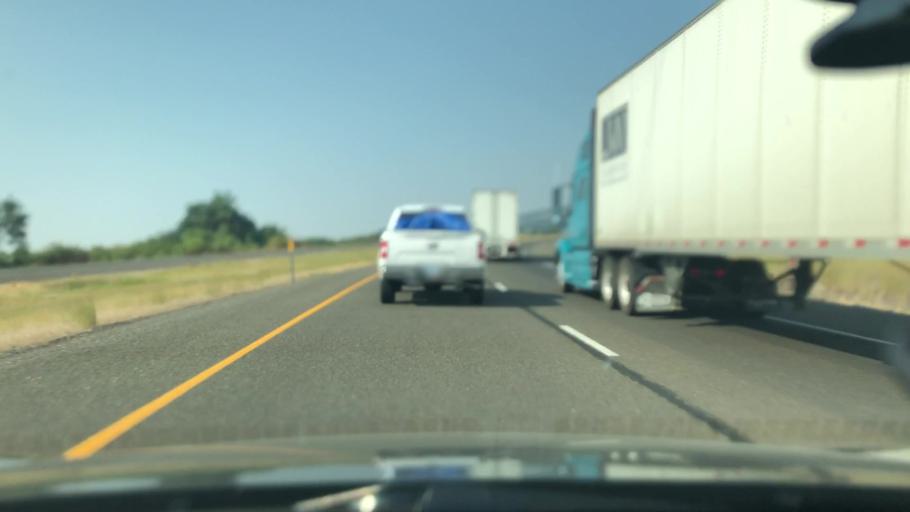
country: US
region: Oregon
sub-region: Union County
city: Union
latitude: 45.1525
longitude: -117.9716
